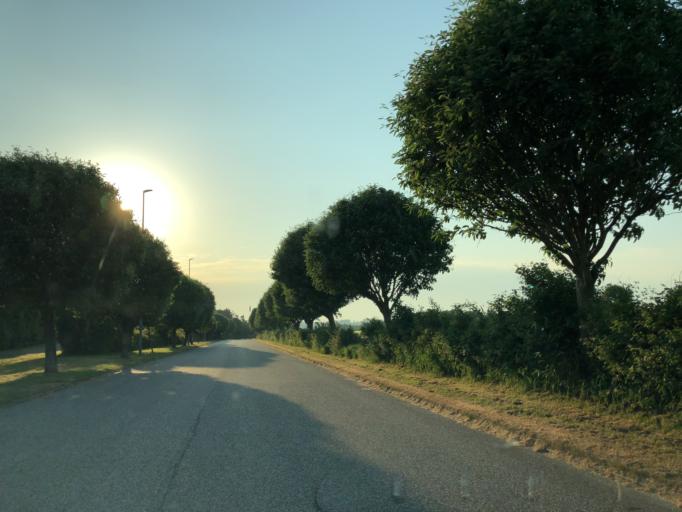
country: DK
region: Central Jutland
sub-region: Struer Kommune
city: Struer
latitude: 56.4848
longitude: 8.5679
